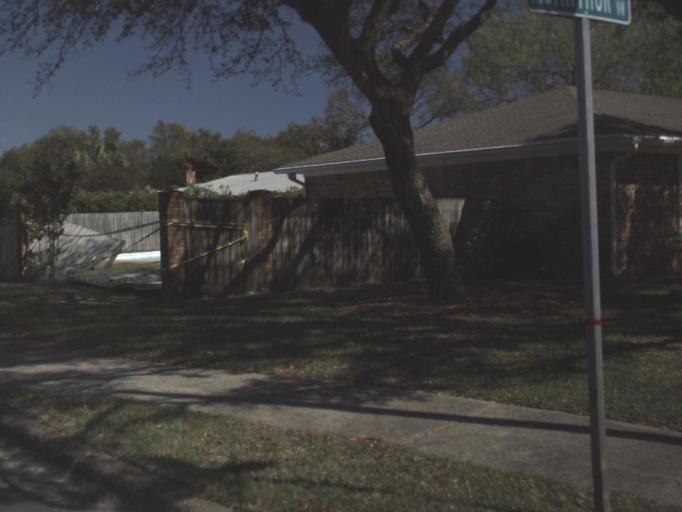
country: US
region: Florida
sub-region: Okaloosa County
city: Ocean City
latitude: 30.4271
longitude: -86.6267
